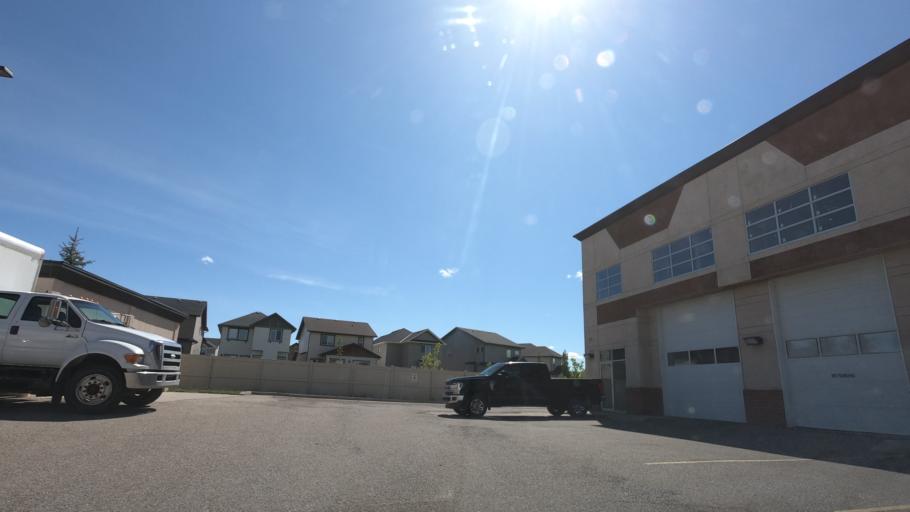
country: CA
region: Alberta
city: Airdrie
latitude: 51.2624
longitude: -113.9936
